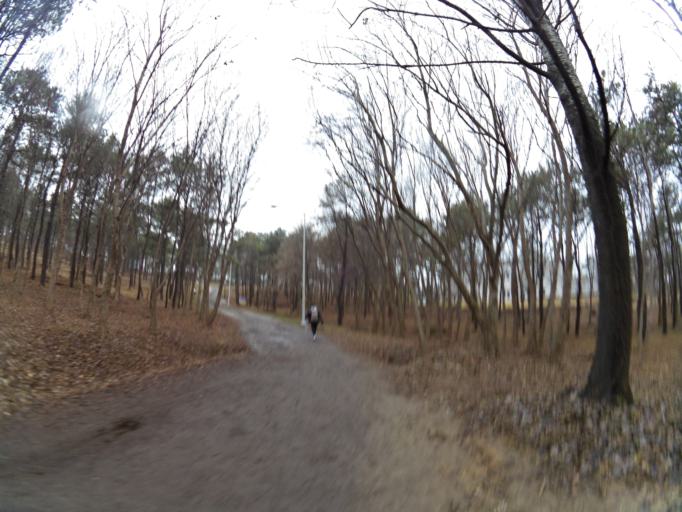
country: KR
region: Gyeongsangbuk-do
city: Gyeongsan-si
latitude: 35.8370
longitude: 128.7577
